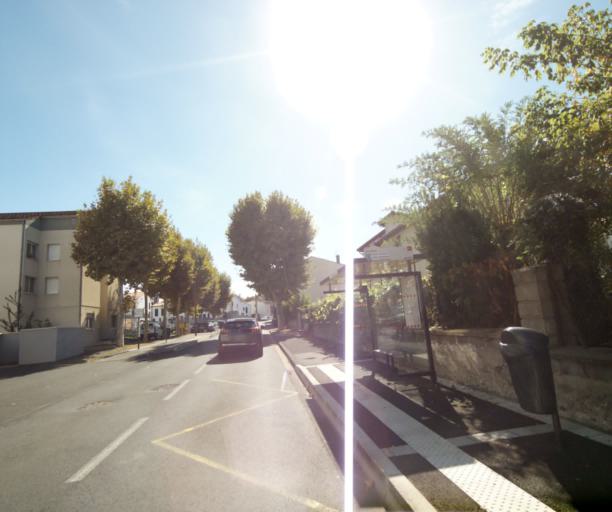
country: FR
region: Auvergne
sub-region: Departement du Puy-de-Dome
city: Cournon-d'Auvergne
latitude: 45.7726
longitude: 3.1961
